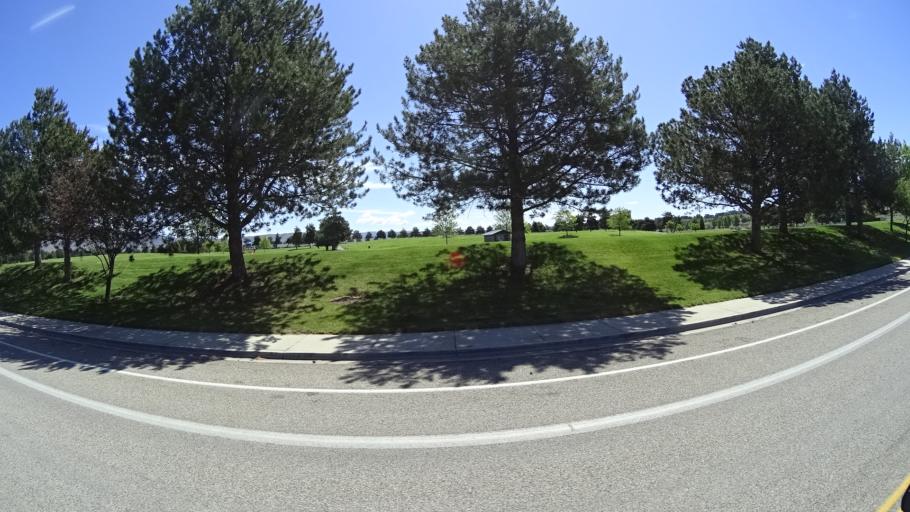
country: US
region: Idaho
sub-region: Ada County
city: Boise
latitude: 43.5488
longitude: -116.1536
